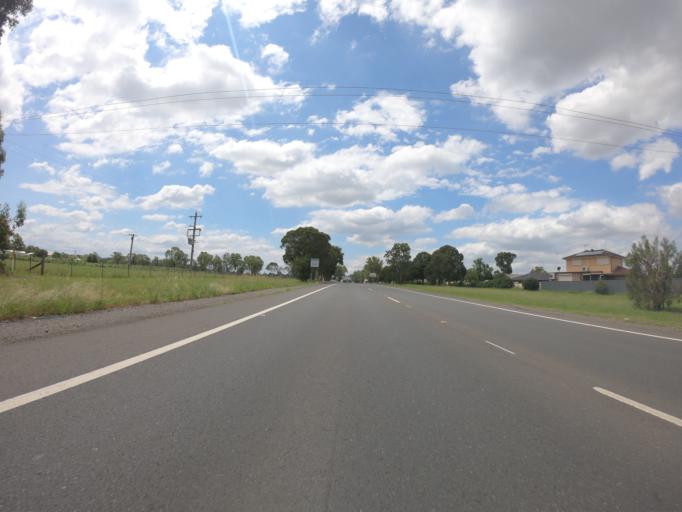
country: AU
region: New South Wales
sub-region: Blacktown
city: Mount Druitt
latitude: -33.7917
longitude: 150.7698
